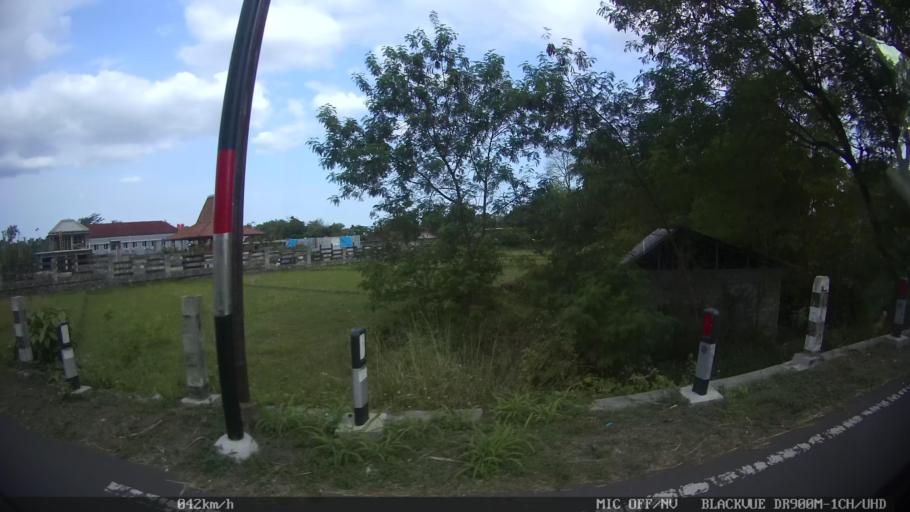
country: ID
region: Daerah Istimewa Yogyakarta
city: Sleman
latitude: -7.6844
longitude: 110.4247
